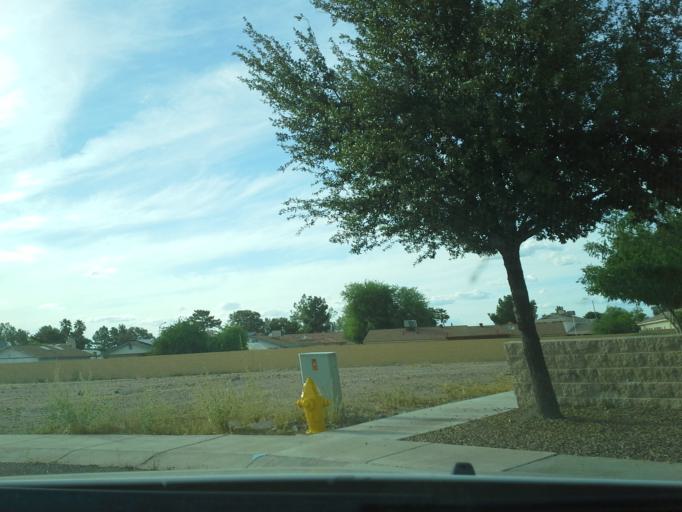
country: US
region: Arizona
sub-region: Maricopa County
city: Peoria
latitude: 33.6430
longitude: -112.2125
